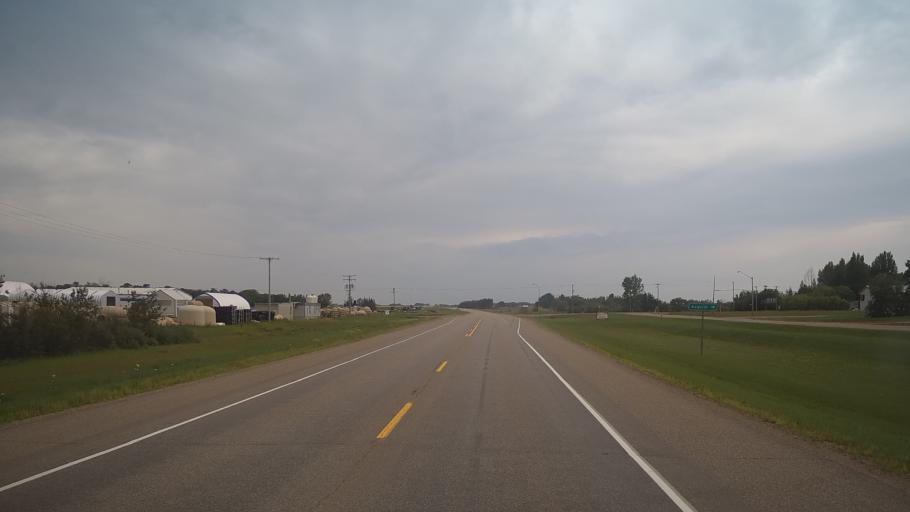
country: CA
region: Saskatchewan
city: Langham
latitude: 52.1289
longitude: -107.2256
